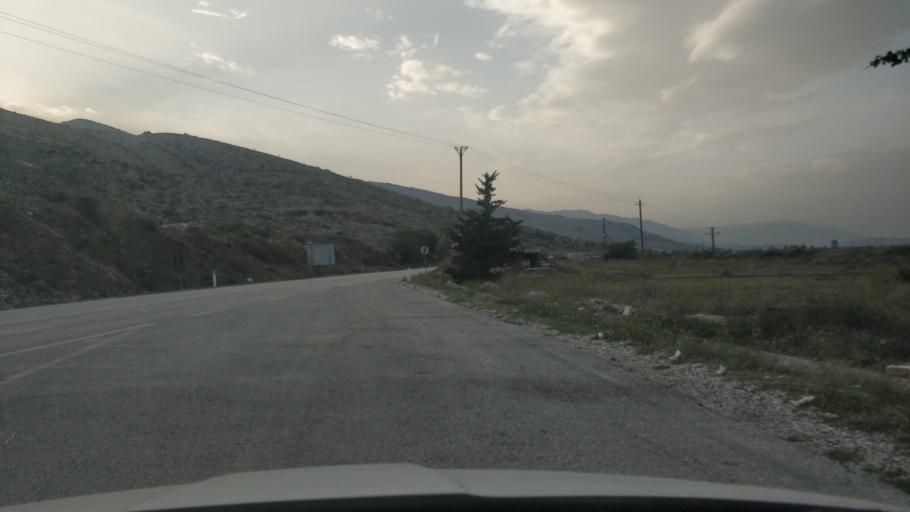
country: AL
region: Gjirokaster
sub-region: Rrethi i Gjirokastres
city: Libohove
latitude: 39.9432
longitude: 20.2649
